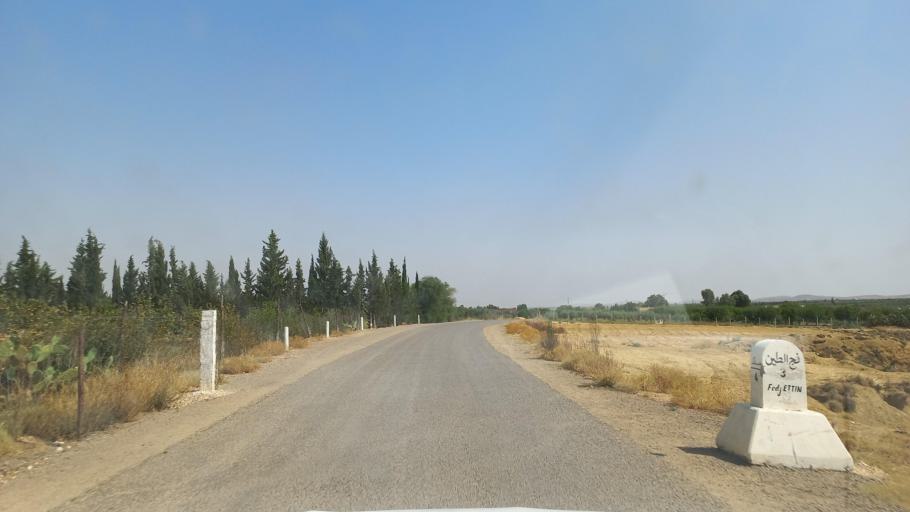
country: TN
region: Al Qasrayn
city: Kasserine
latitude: 35.2402
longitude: 9.0304
